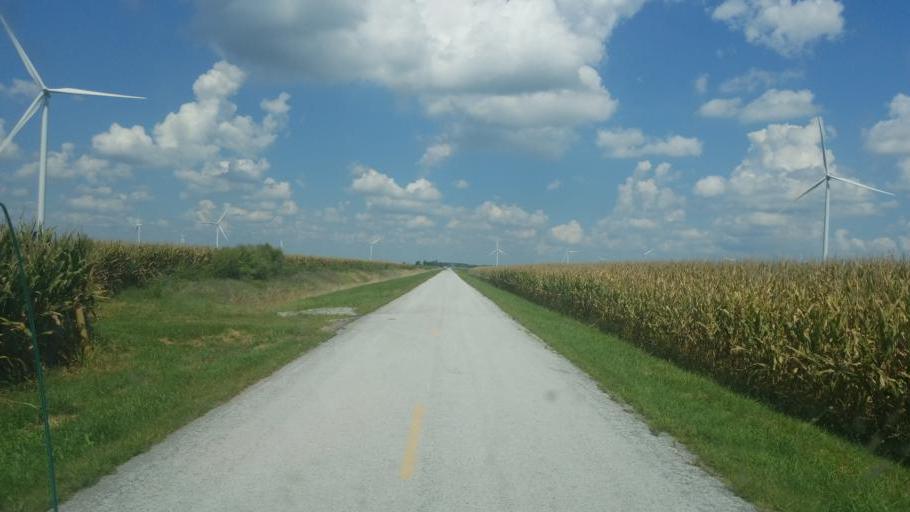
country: US
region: Ohio
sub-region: Hardin County
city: Ada
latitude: 40.7665
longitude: -83.7287
